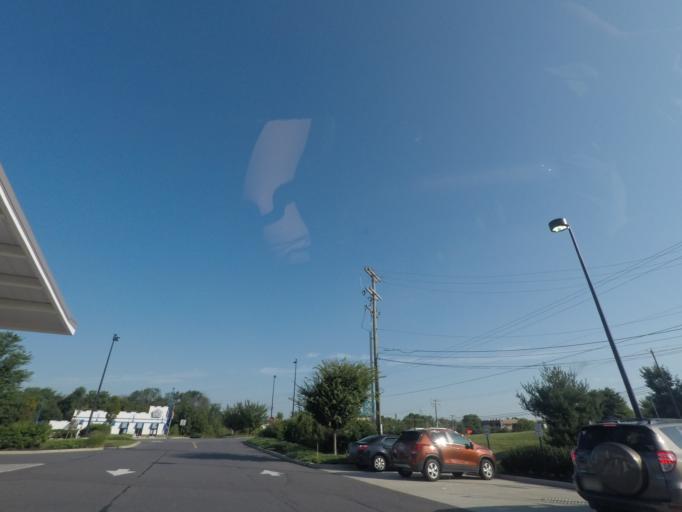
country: US
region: New Jersey
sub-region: Warren County
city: Alpha
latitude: 40.6759
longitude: -75.1417
